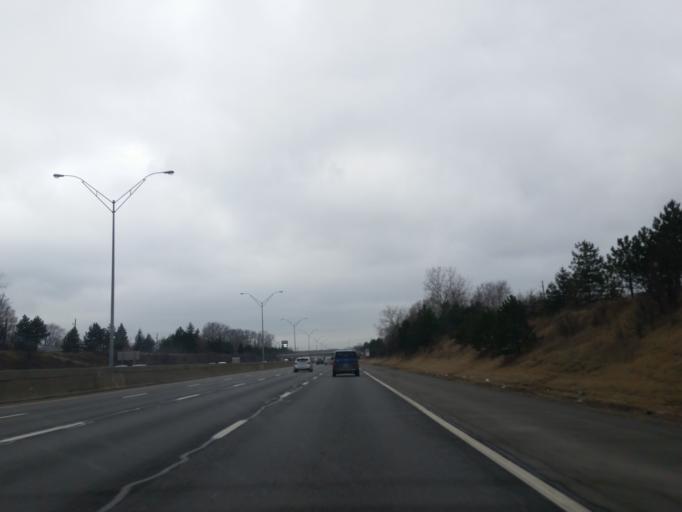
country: US
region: Ohio
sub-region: Cuyahoga County
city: Brooklyn
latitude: 41.4233
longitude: -81.7441
